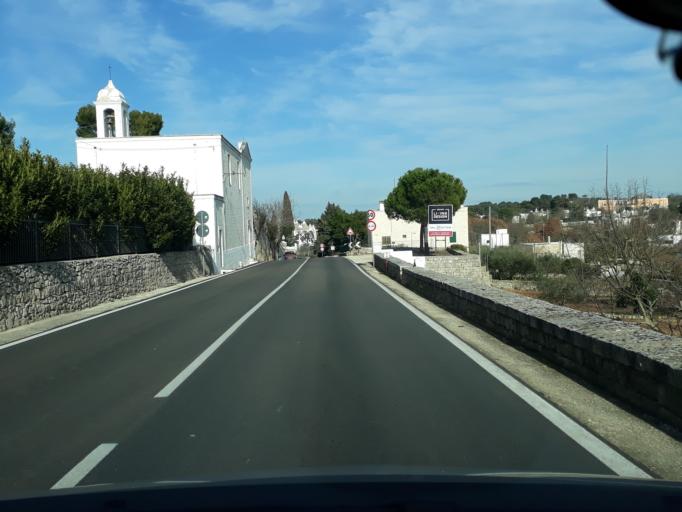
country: IT
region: Apulia
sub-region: Provincia di Brindisi
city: Lamie di Olimpie-Selva
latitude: 40.7930
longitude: 17.3475
